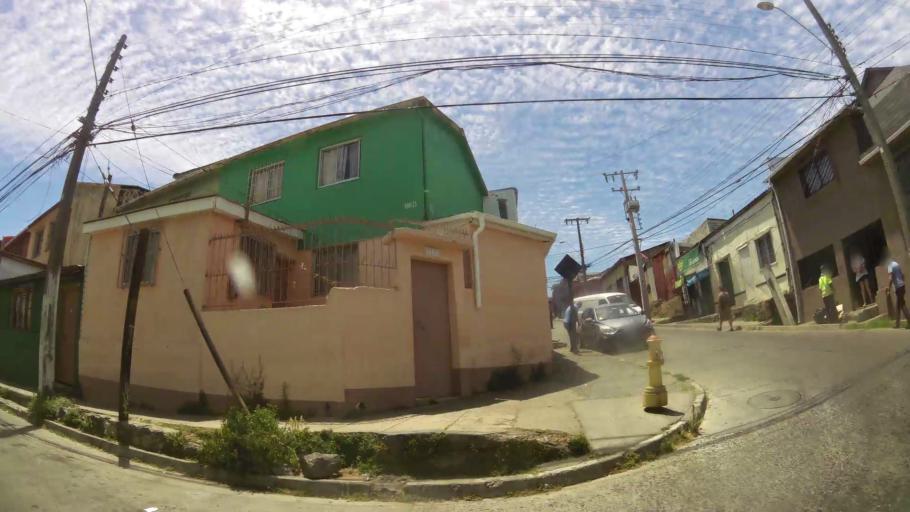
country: CL
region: Valparaiso
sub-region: Provincia de Valparaiso
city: Valparaiso
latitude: -33.0471
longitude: -71.5962
